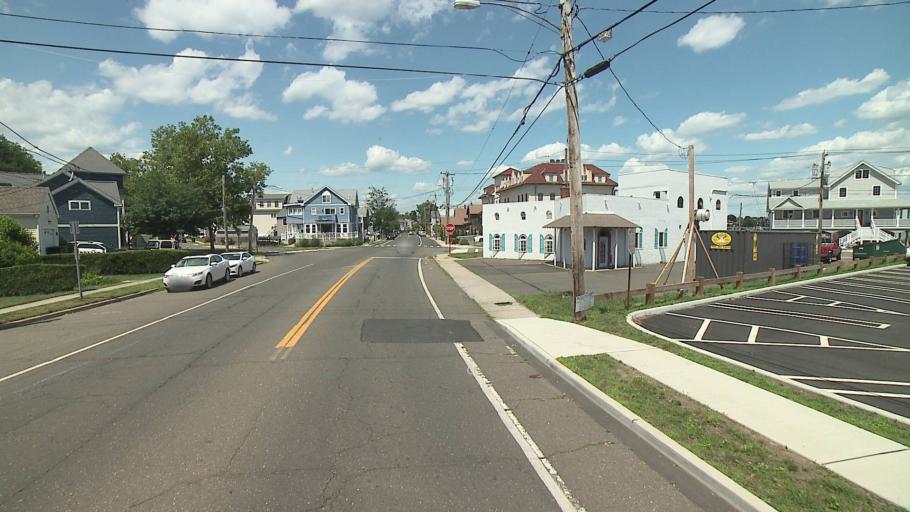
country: US
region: Connecticut
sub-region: New Haven County
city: Woodmont
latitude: 41.2207
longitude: -73.0057
